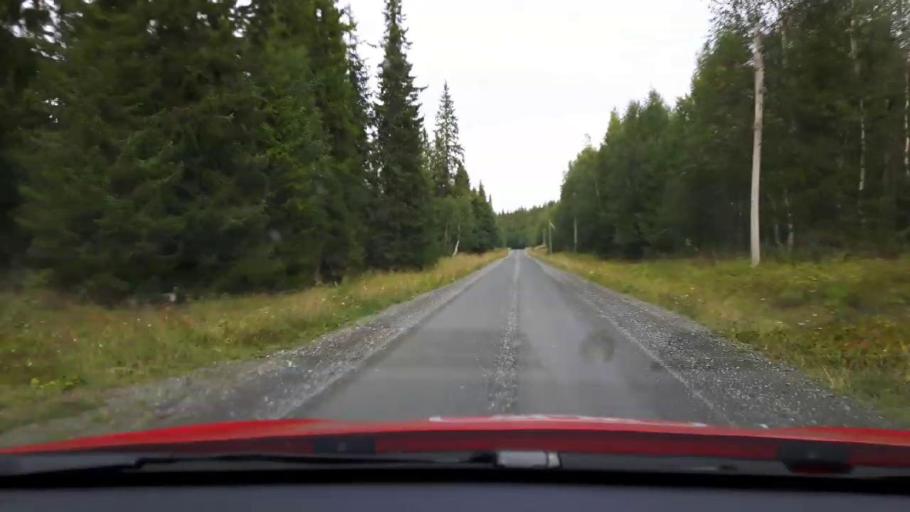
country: SE
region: Jaemtland
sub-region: Are Kommun
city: Are
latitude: 63.7533
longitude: 13.0904
